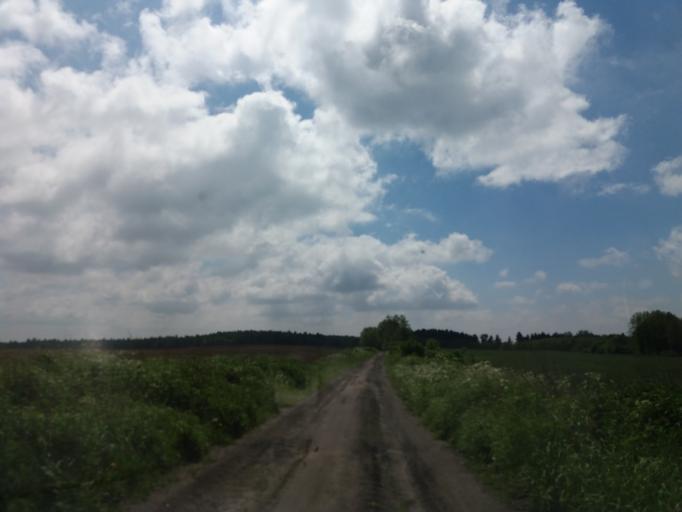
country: PL
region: West Pomeranian Voivodeship
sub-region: Powiat choszczenski
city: Recz
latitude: 53.2763
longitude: 15.5346
